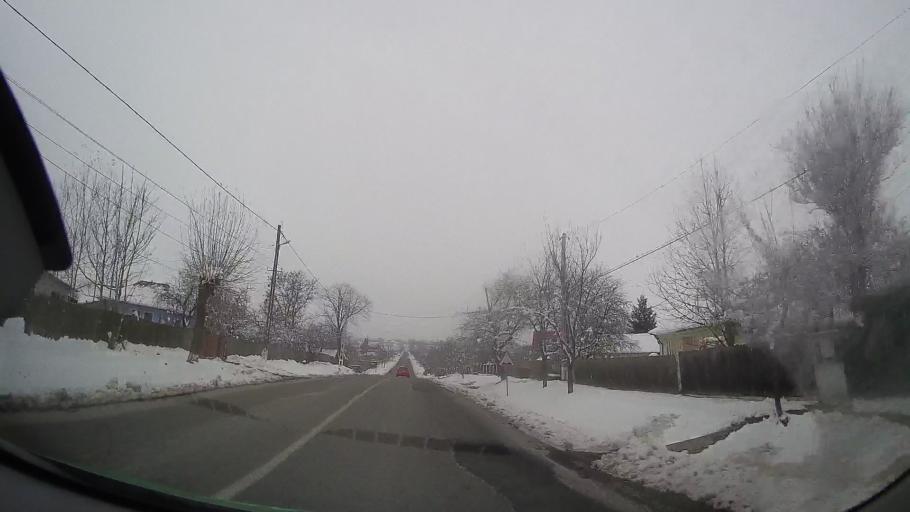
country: RO
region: Vaslui
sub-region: Comuna Negresti
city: Negresti
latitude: 46.8389
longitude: 27.4079
